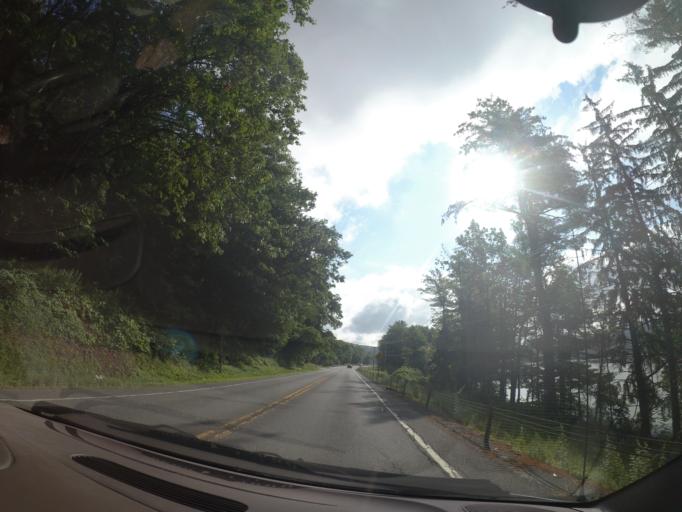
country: US
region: New York
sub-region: Rensselaer County
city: Poestenkill
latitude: 42.8186
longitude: -73.5254
